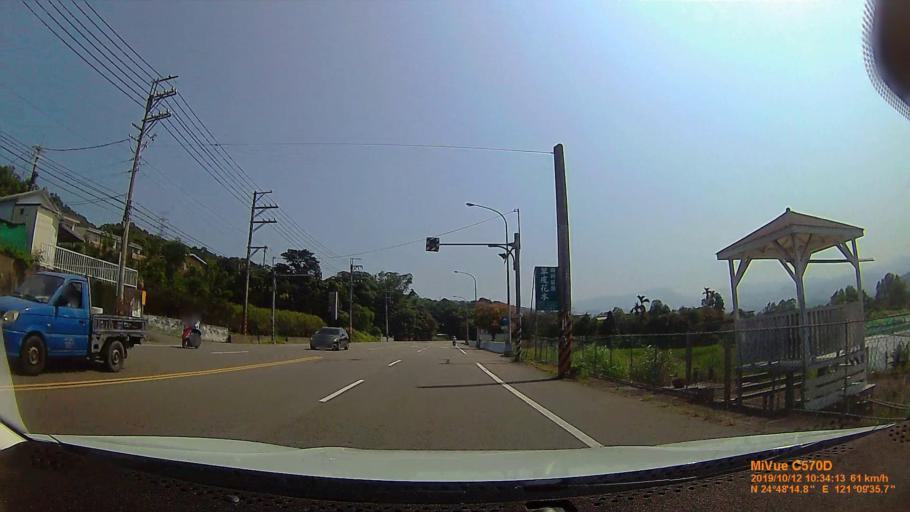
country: TW
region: Taiwan
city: Daxi
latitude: 24.8040
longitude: 121.1598
